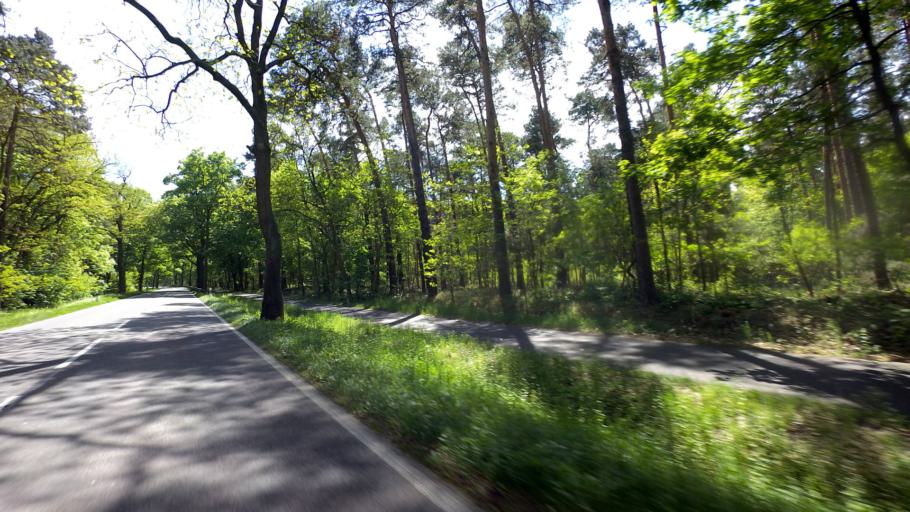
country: DE
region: Brandenburg
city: Luckenwalde
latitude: 52.0677
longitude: 13.2028
